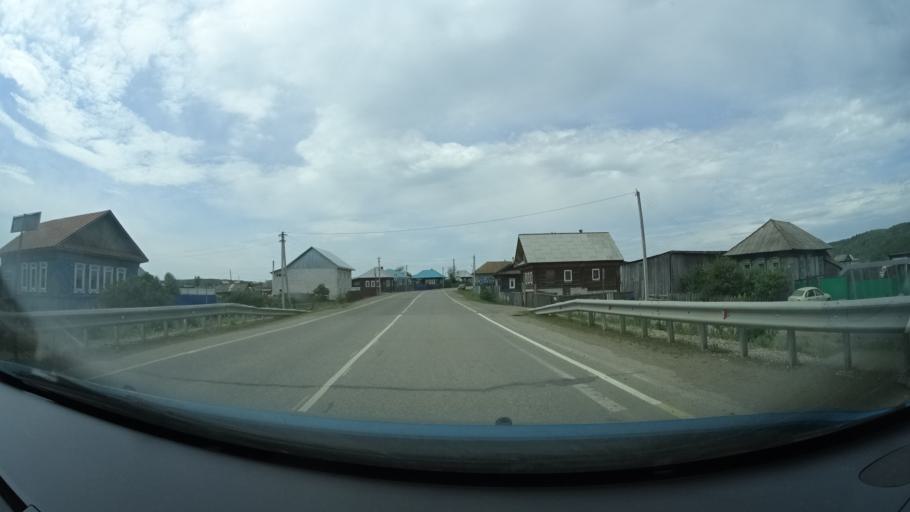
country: RU
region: Perm
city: Barda
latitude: 56.8229
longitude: 55.6307
